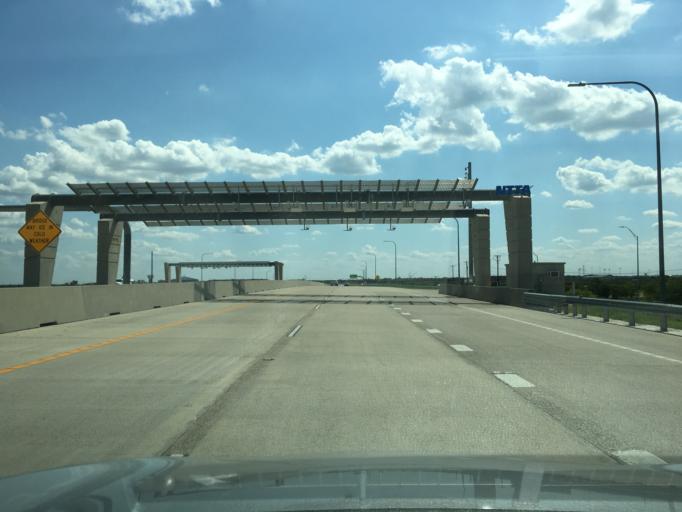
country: US
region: Texas
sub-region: Tarrant County
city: Mansfield
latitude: 32.6287
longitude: -97.0683
